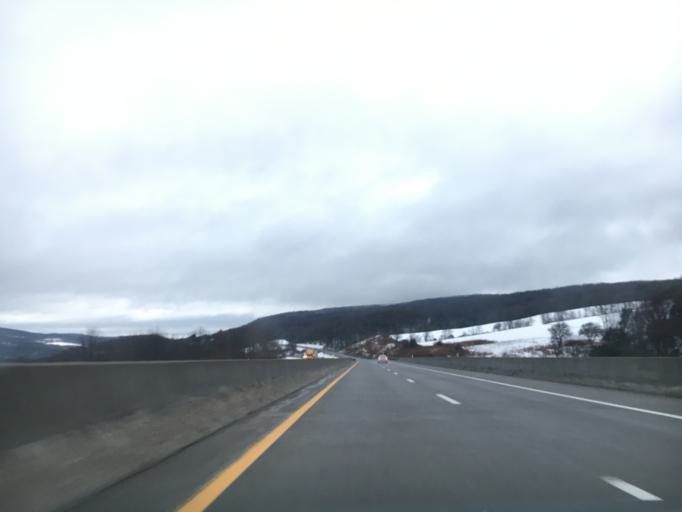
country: US
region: New York
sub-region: Cortland County
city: McGraw
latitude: 42.5465
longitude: -76.0937
